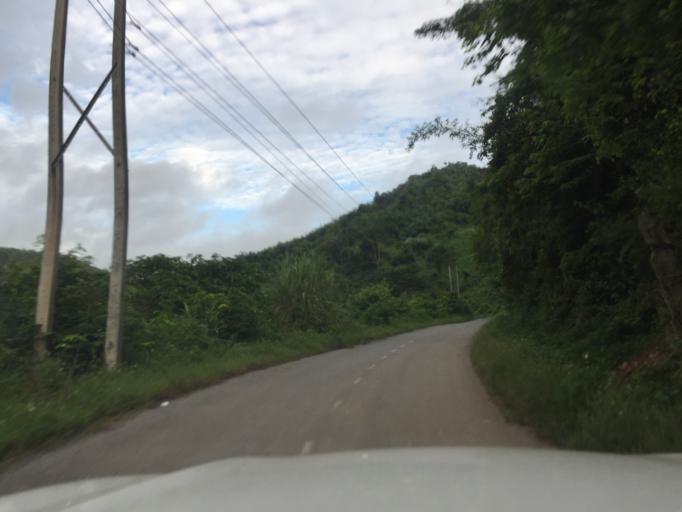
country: LA
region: Phongsali
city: Khoa
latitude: 21.1013
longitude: 102.2803
